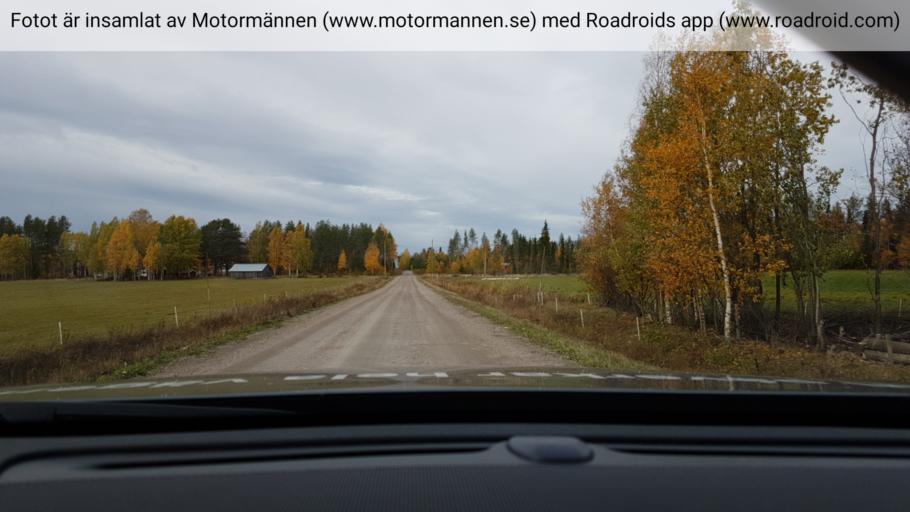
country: SE
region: Norrbotten
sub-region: Overkalix Kommun
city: OEverkalix
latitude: 66.3026
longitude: 22.9293
